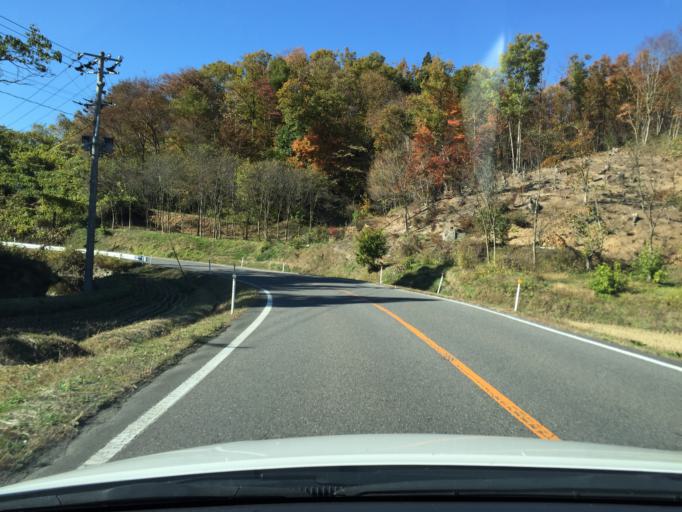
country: JP
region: Fukushima
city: Miharu
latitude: 37.4181
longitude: 140.5322
